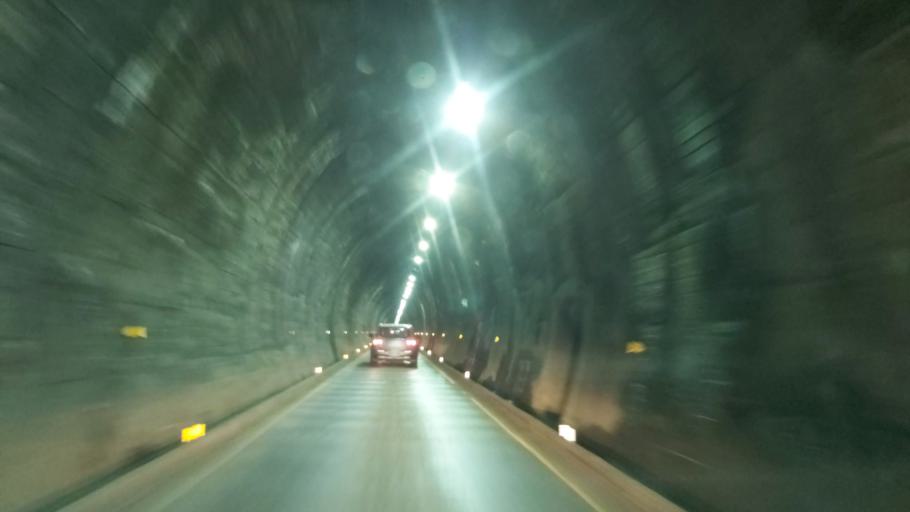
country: CL
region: Araucania
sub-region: Provincia de Cautin
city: Vilcun
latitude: -38.5185
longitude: -71.5161
